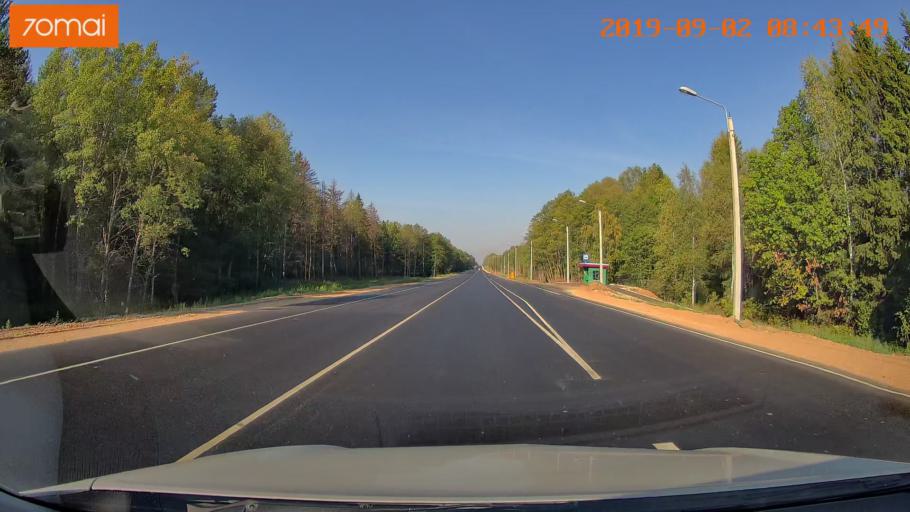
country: RU
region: Kaluga
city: Medyn'
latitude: 54.9712
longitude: 36.0510
